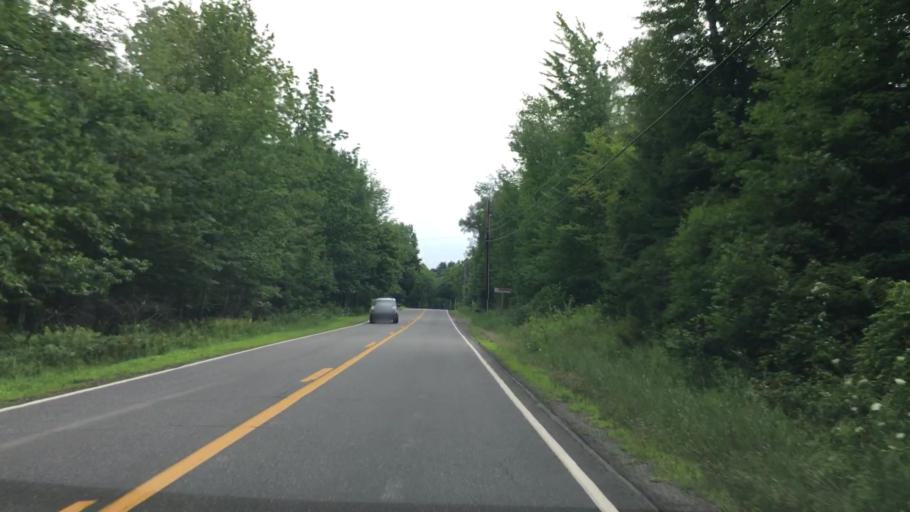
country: US
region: Maine
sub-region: Waldo County
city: Belfast
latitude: 44.3552
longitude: -69.0509
